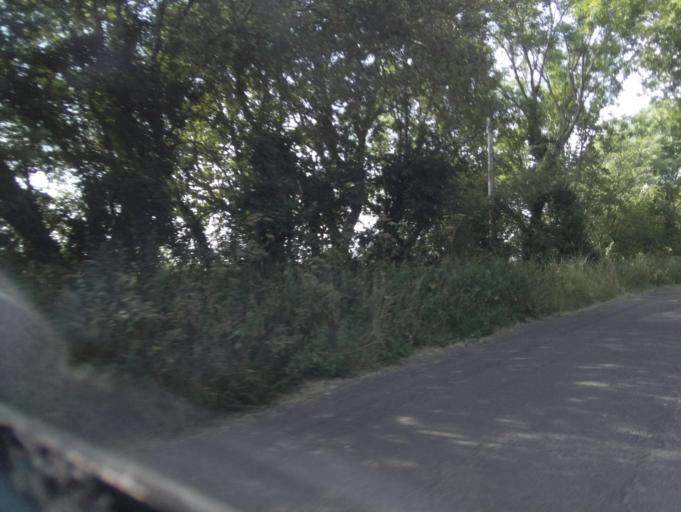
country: GB
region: England
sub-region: Wiltshire
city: Minety
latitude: 51.6319
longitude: -1.9752
